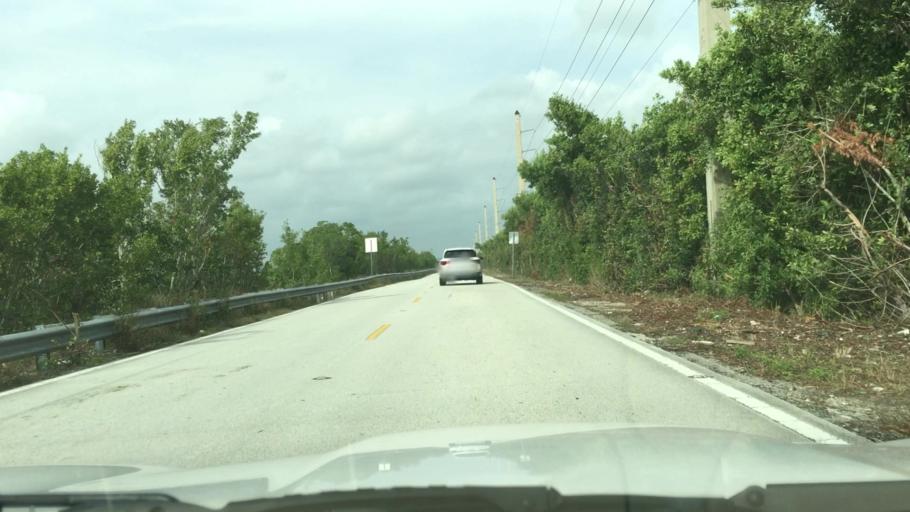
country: US
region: Florida
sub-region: Monroe County
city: North Key Largo
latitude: 25.3020
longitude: -80.3876
